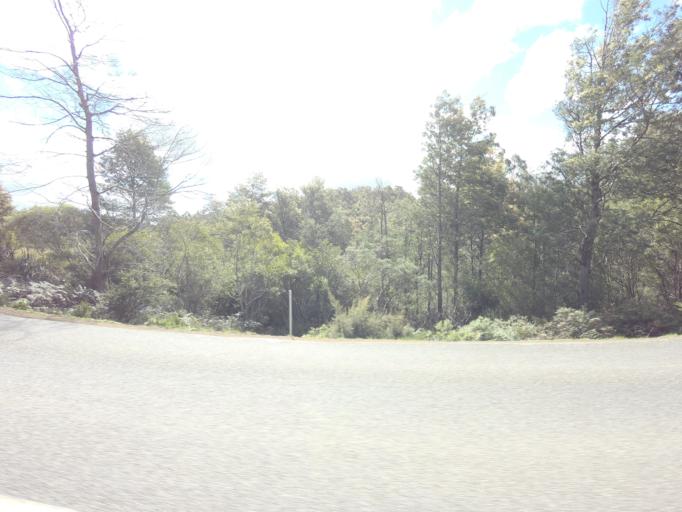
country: AU
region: Tasmania
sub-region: Huon Valley
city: Geeveston
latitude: -43.1978
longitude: 146.9510
